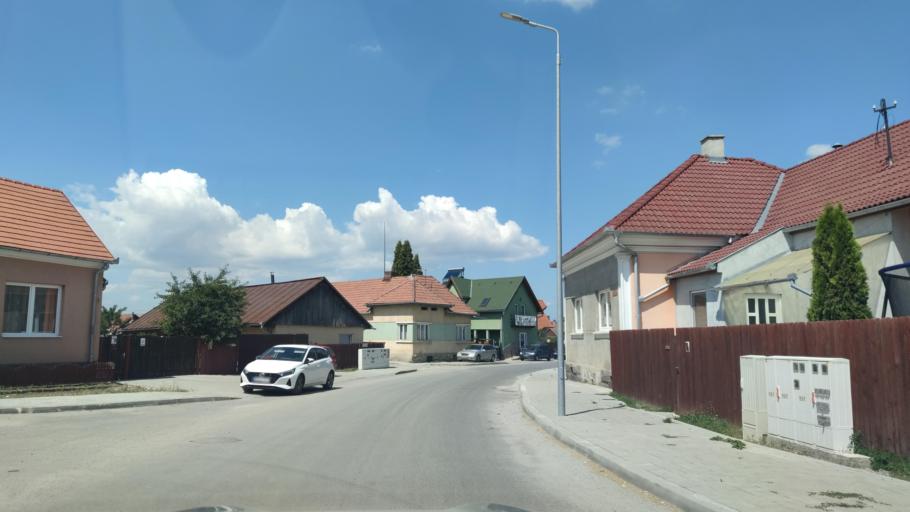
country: RO
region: Harghita
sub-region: Municipiul Gheorgheni
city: Gheorgheni
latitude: 46.7183
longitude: 25.5996
